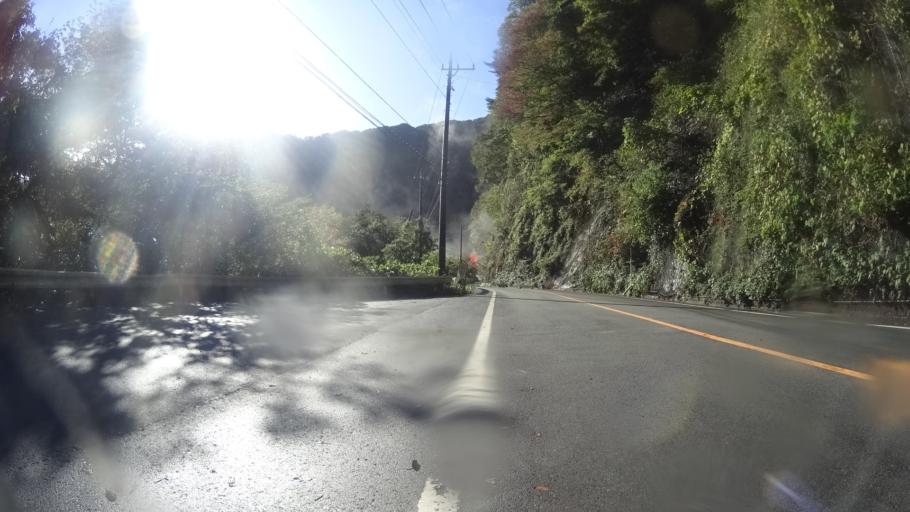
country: JP
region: Yamanashi
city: Otsuki
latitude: 35.7876
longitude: 138.9590
